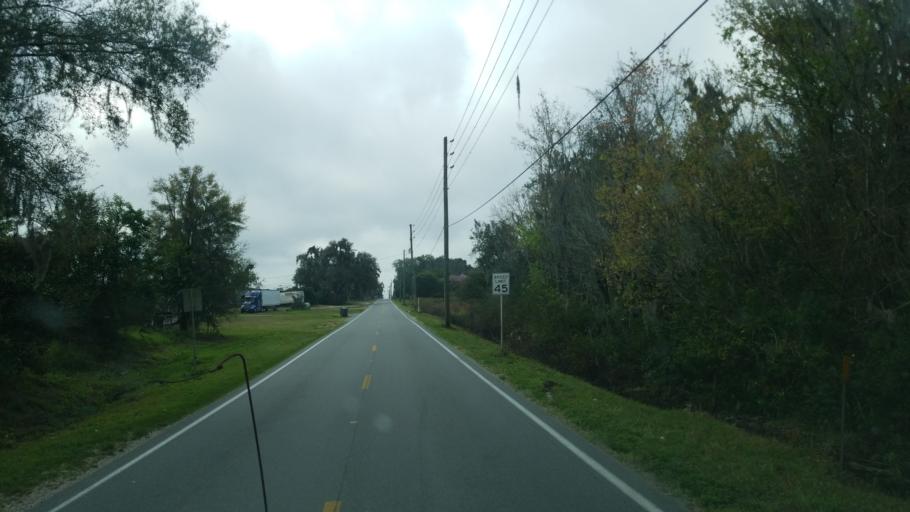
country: US
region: Florida
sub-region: Polk County
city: Kathleen
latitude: 28.1481
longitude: -82.0233
